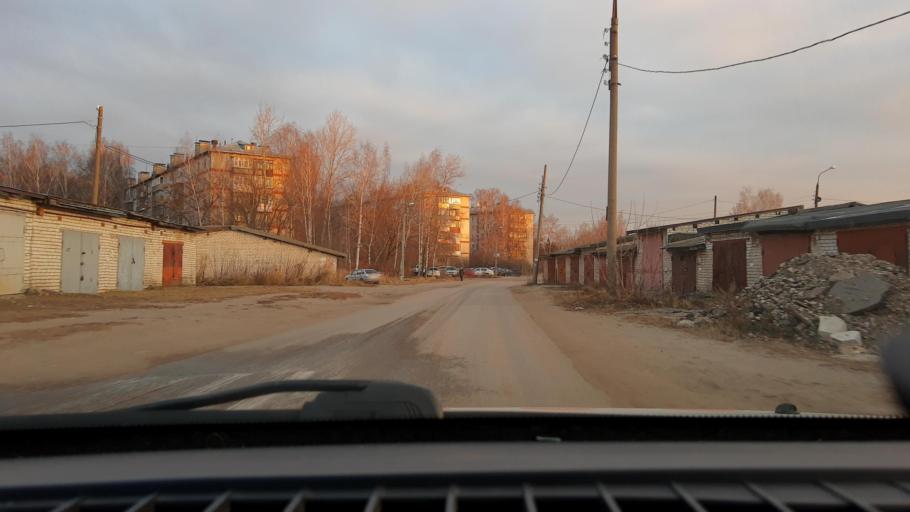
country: RU
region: Nizjnij Novgorod
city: Gorbatovka
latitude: 56.3267
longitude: 43.8390
